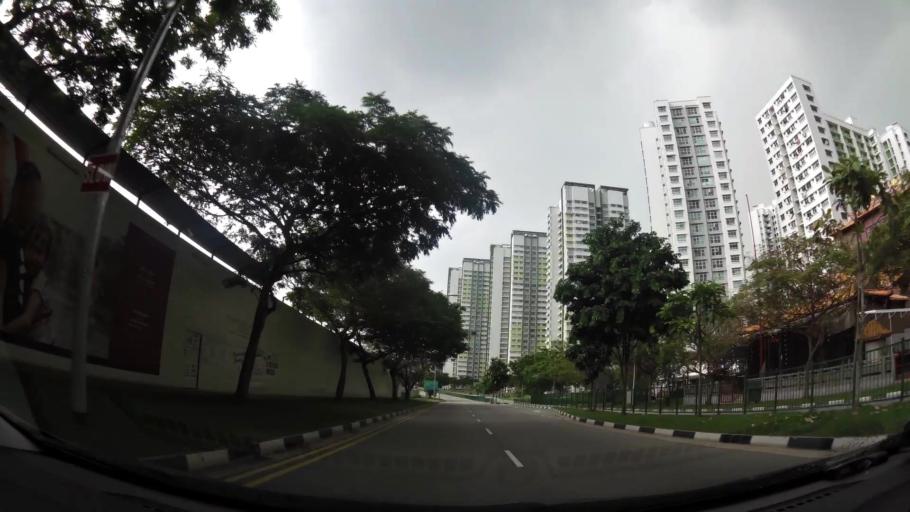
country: MY
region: Johor
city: Kampung Pasir Gudang Baru
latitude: 1.3919
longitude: 103.8718
